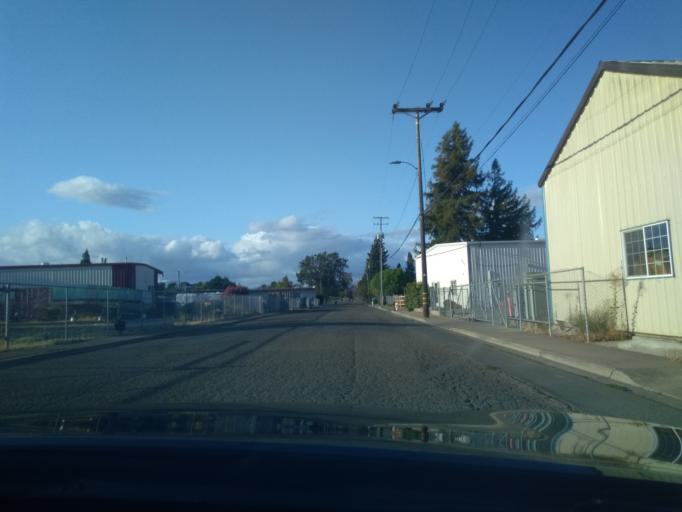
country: US
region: California
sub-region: Mendocino County
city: Ukiah
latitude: 39.1600
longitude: -123.2073
